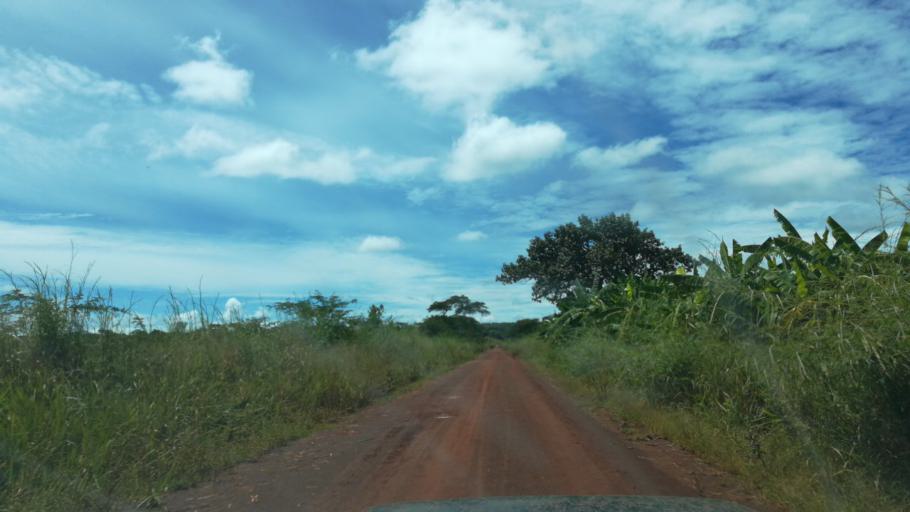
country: ZM
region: Luapula
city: Nchelenge
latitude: -9.7656
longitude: 28.1796
